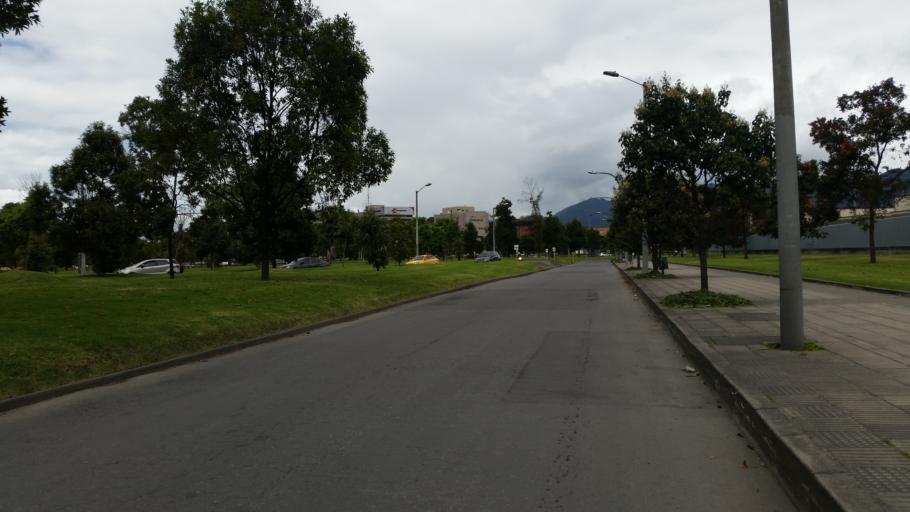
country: CO
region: Bogota D.C.
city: Bogota
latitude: 4.6511
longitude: -74.1046
